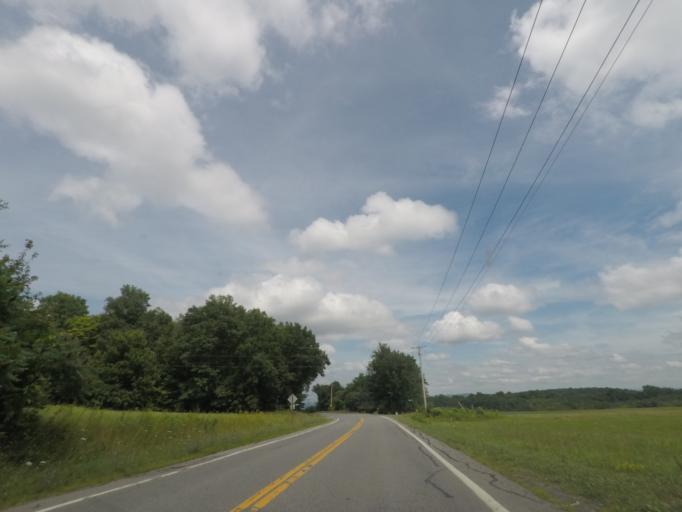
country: US
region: New York
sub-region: Saratoga County
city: Stillwater
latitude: 43.0235
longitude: -73.6710
